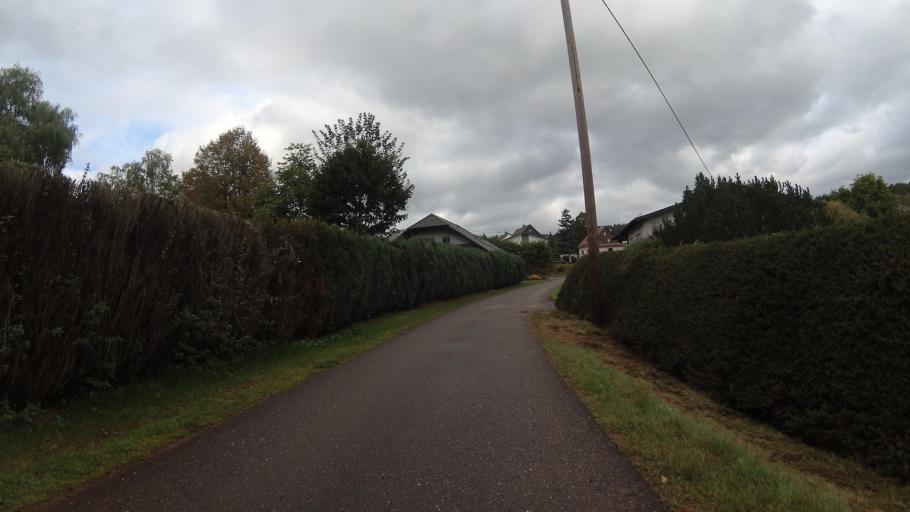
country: DE
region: Saarland
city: Oberthal
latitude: 49.5161
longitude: 7.1057
